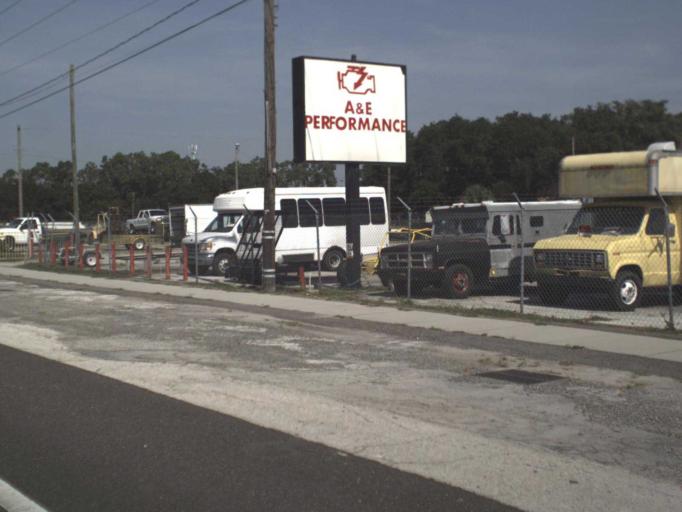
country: US
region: Florida
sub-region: Hillsborough County
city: Plant City
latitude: 27.9378
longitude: -82.1163
